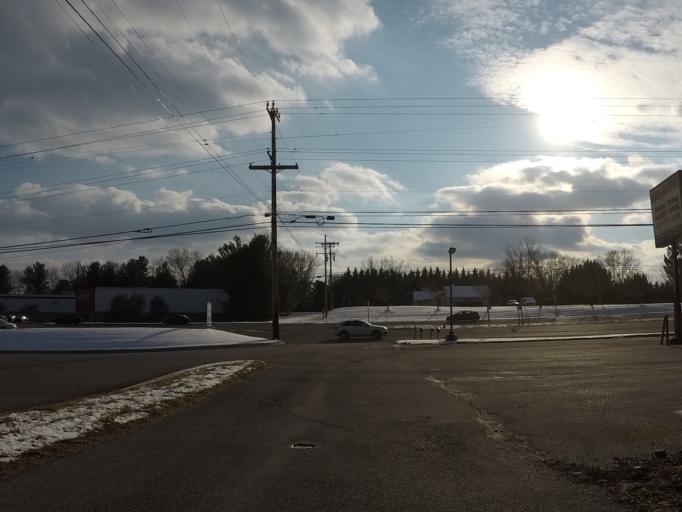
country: US
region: Maryland
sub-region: Howard County
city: Columbia
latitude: 39.2818
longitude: -76.8717
